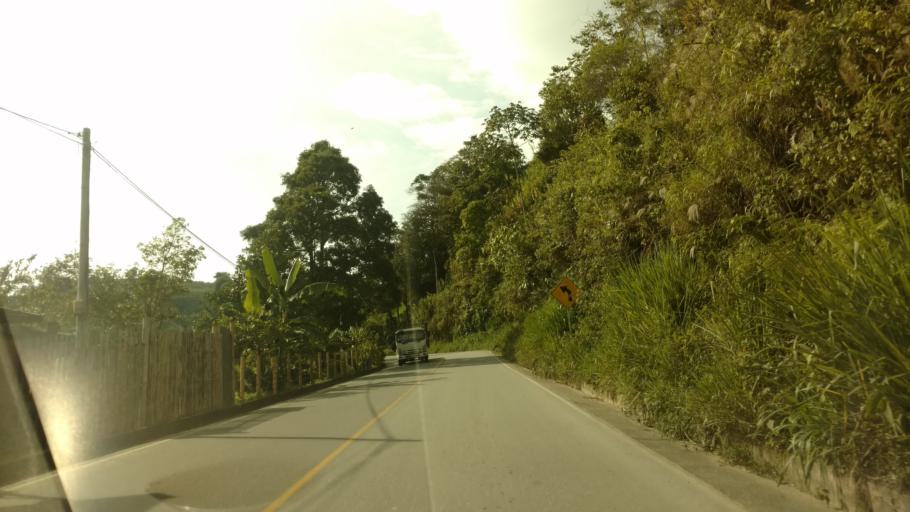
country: CO
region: Caldas
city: Neira
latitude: 5.1374
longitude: -75.5020
